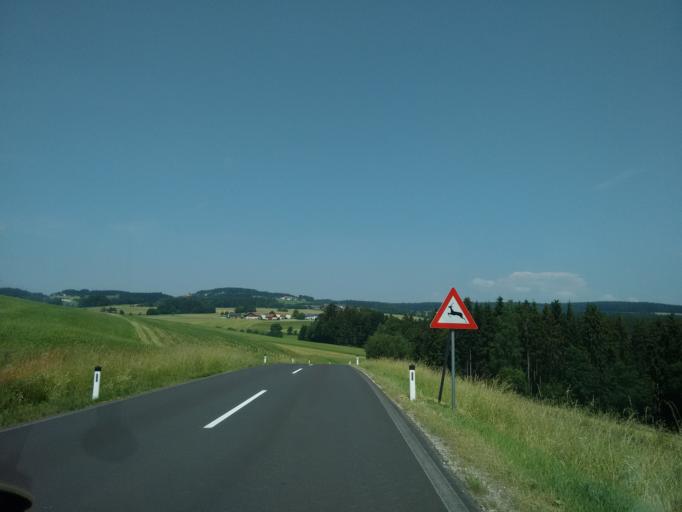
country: AT
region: Upper Austria
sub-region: Politischer Bezirk Urfahr-Umgebung
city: Altenberg bei Linz
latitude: 48.3971
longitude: 14.3458
